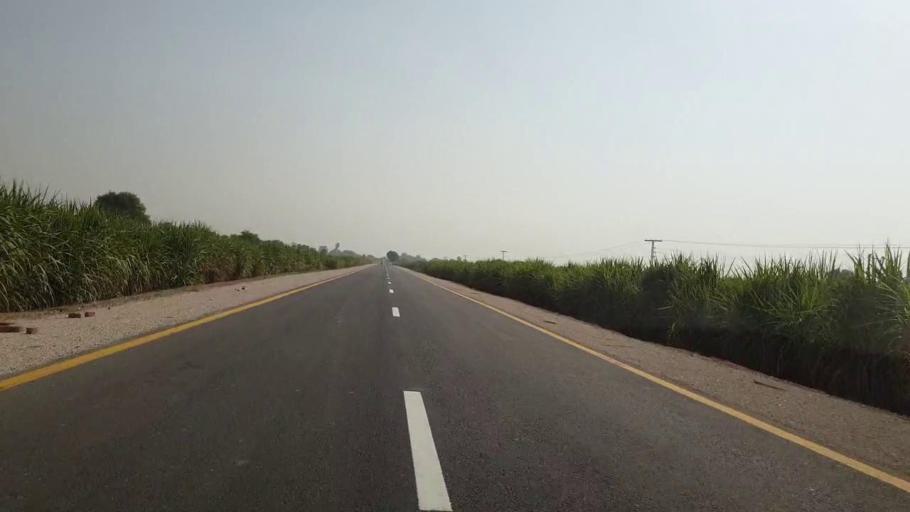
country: PK
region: Sindh
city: Bhan
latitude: 26.6103
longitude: 67.7787
